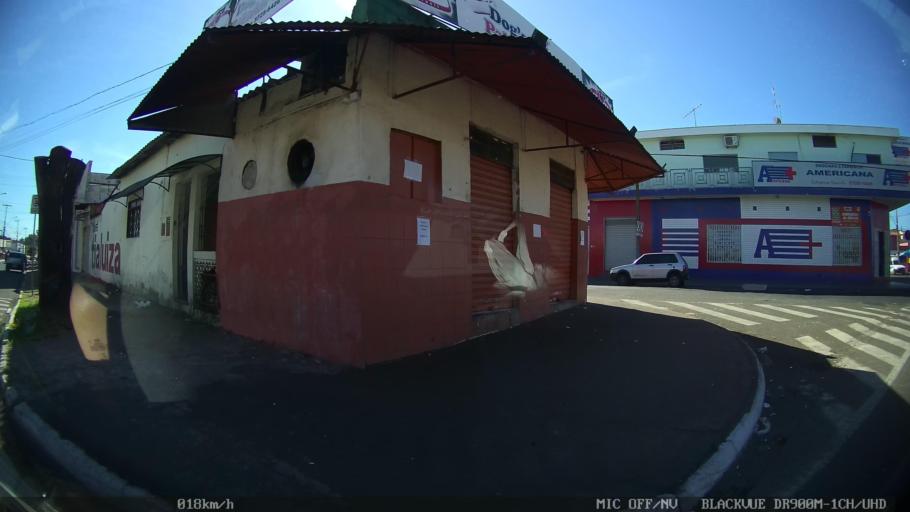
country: BR
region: Sao Paulo
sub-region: Franca
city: Franca
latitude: -20.5257
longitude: -47.3695
